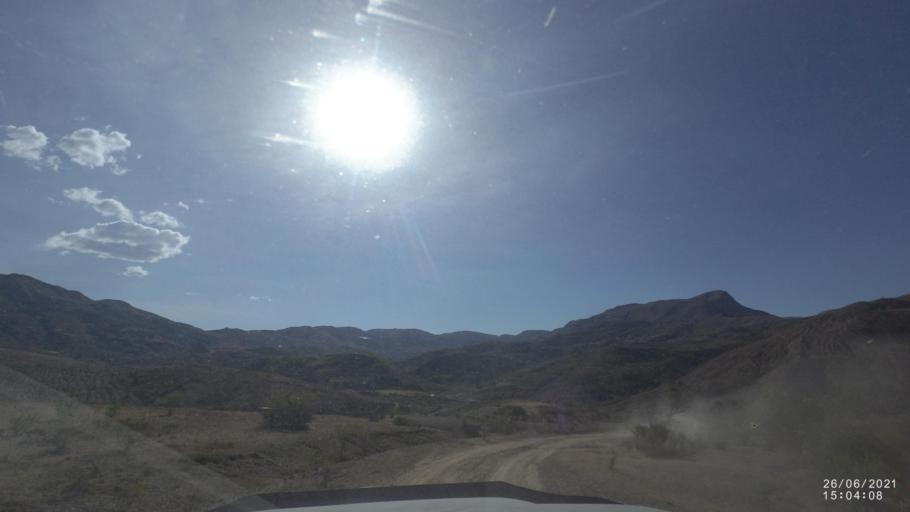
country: BO
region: Cochabamba
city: Mizque
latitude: -17.9468
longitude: -65.6318
